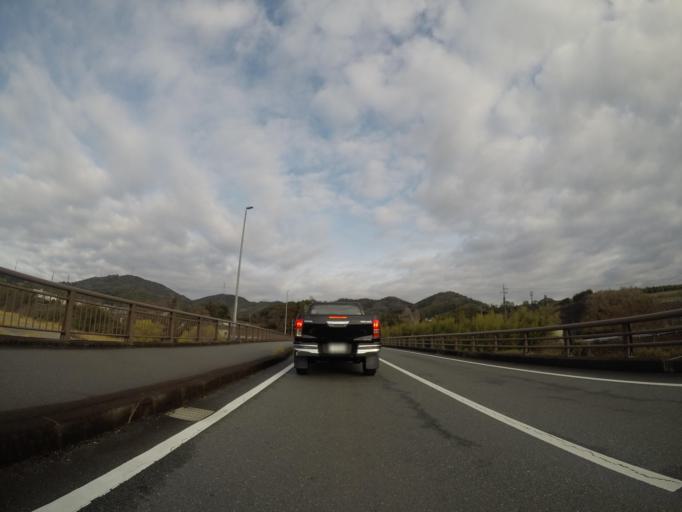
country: JP
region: Shizuoka
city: Hamakita
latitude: 34.8282
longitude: 137.7231
